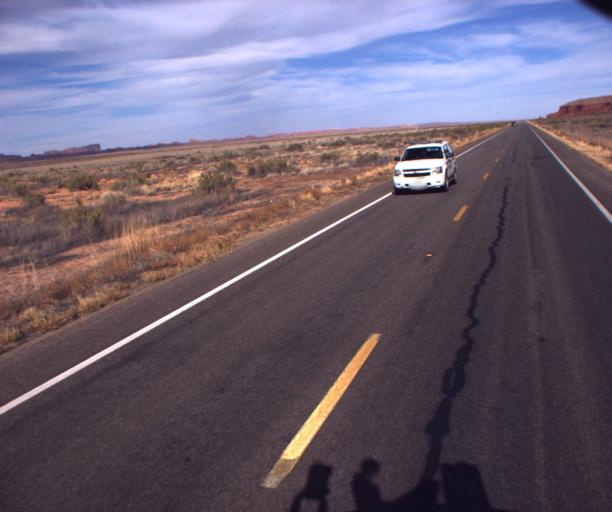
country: US
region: Arizona
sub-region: Navajo County
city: Kayenta
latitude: 36.7561
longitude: -110.0520
